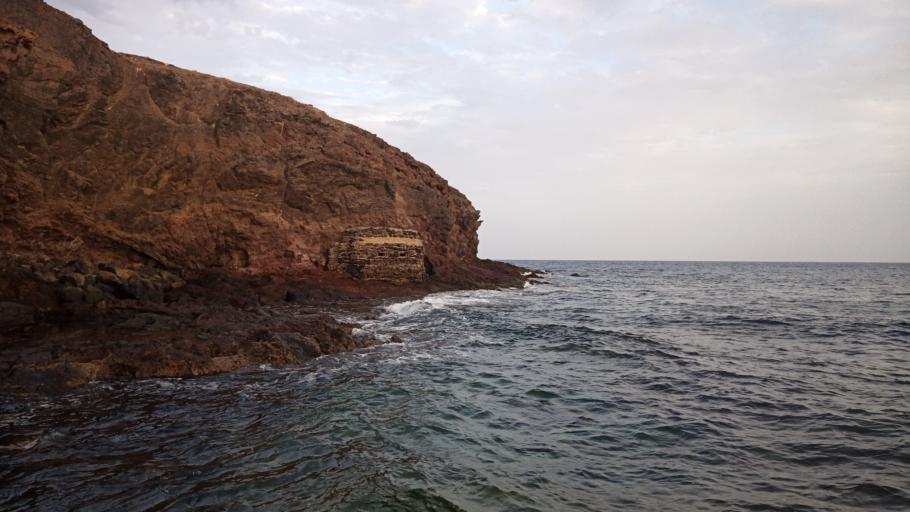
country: ES
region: Canary Islands
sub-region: Provincia de Las Palmas
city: Playa Blanca
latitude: 28.8438
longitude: -13.7805
